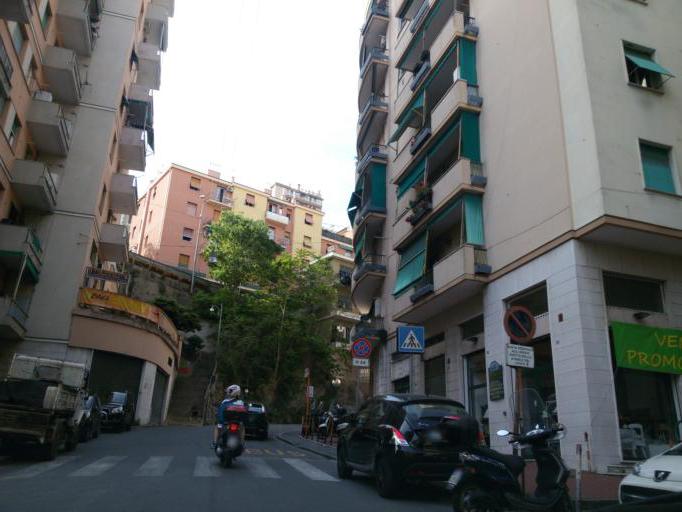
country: IT
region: Liguria
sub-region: Provincia di Genova
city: Genoa
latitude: 44.4193
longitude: 8.9572
